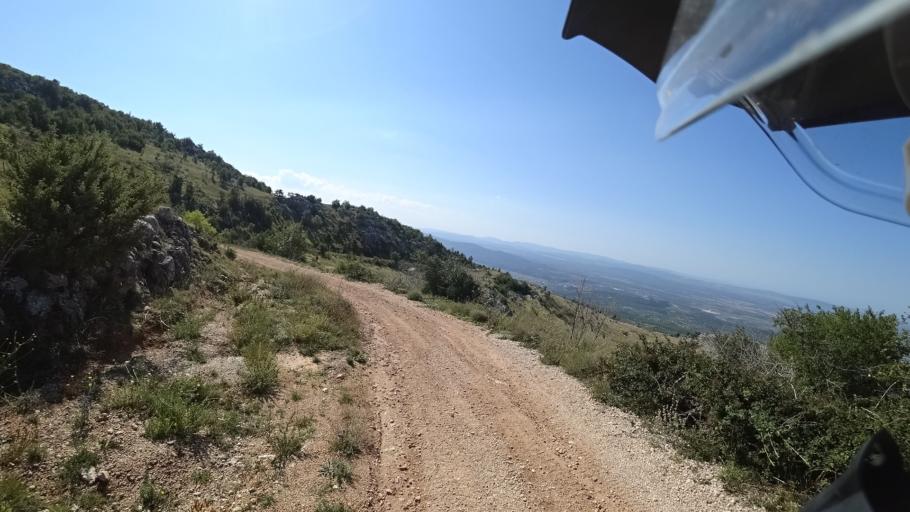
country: HR
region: Sibensko-Kniniska
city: Drnis
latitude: 43.9197
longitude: 16.1679
